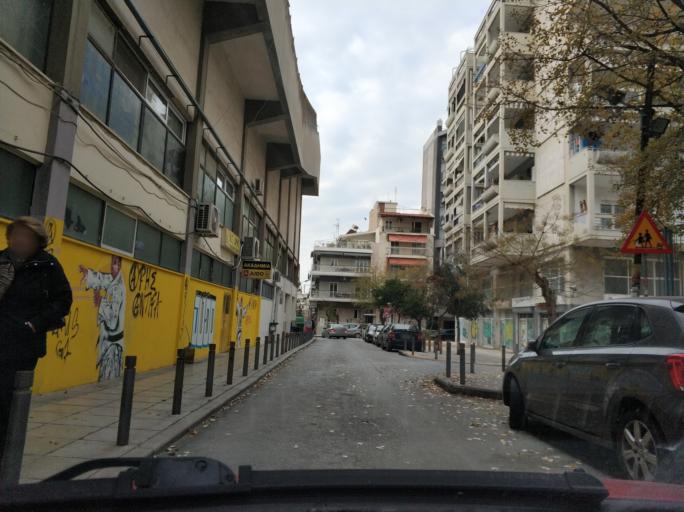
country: GR
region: Central Macedonia
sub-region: Nomos Thessalonikis
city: Triandria
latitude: 40.6008
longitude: 22.9690
